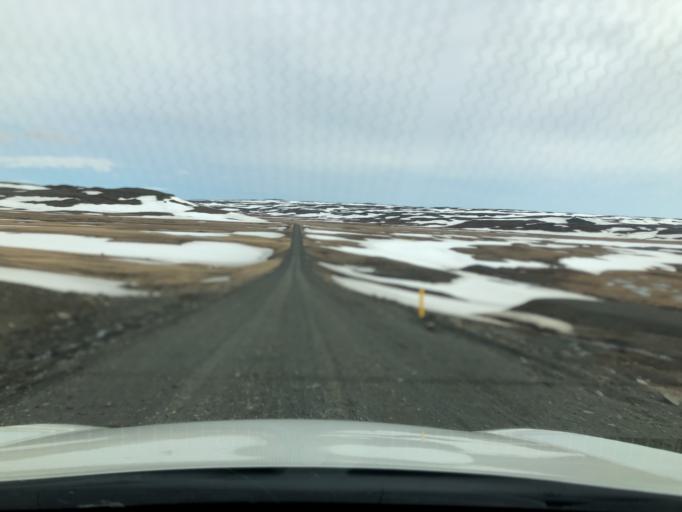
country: IS
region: East
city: Egilsstadir
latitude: 65.2946
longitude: -15.4445
